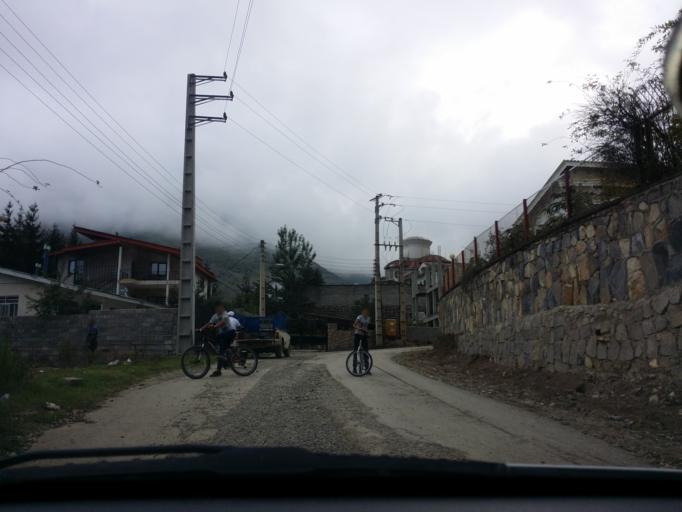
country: IR
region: Mazandaran
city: `Abbasabad
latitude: 36.4895
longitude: 51.1368
